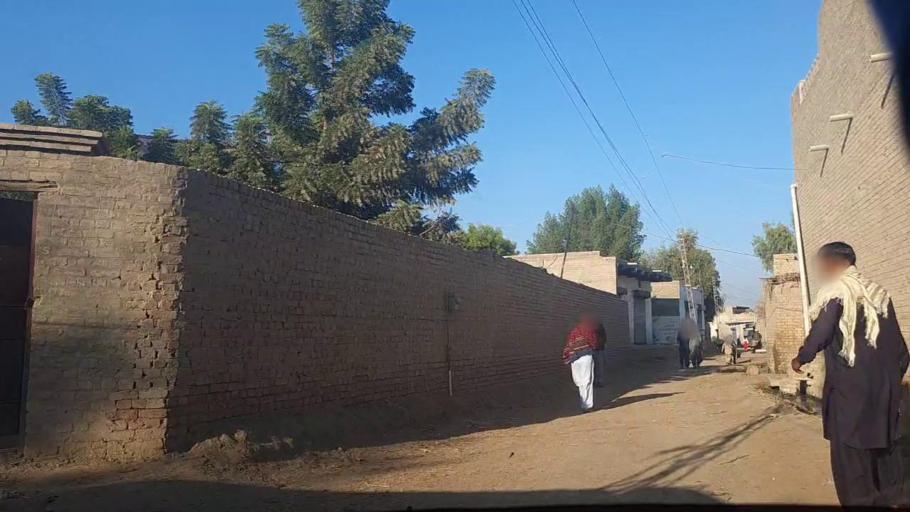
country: PK
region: Sindh
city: Sobhadero
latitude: 27.3976
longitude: 68.4205
